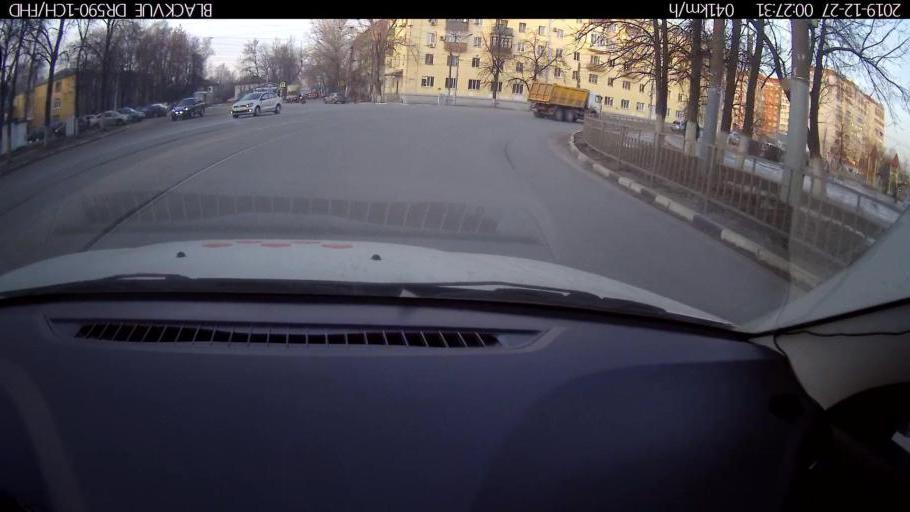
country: RU
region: Nizjnij Novgorod
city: Nizhniy Novgorod
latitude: 56.3130
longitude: 43.9361
